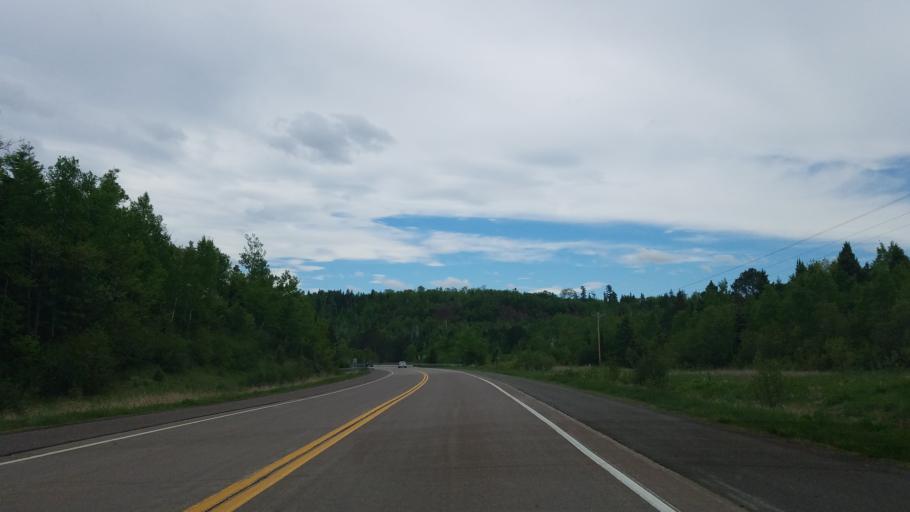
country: US
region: Minnesota
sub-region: Lake County
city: Two Harbors
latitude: 47.1026
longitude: -91.5415
